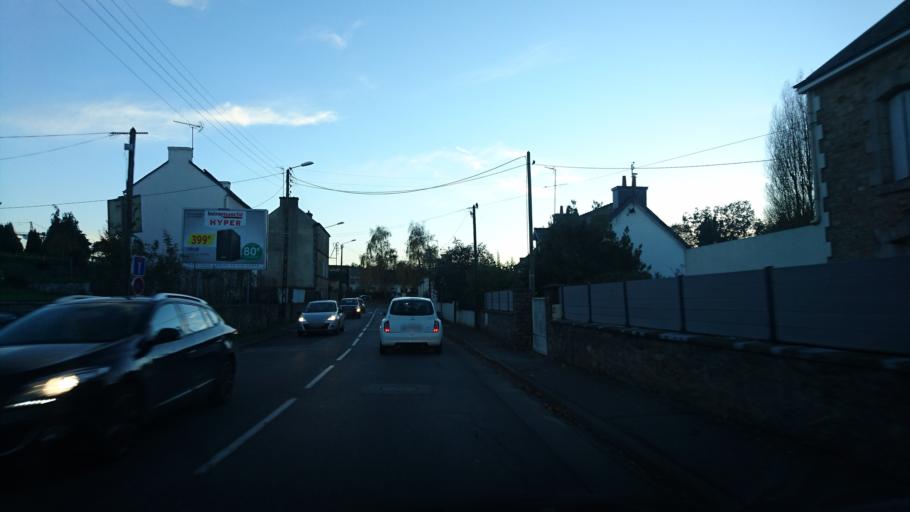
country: FR
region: Brittany
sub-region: Departement du Finistere
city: Quimperle
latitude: 47.8668
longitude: -3.5550
